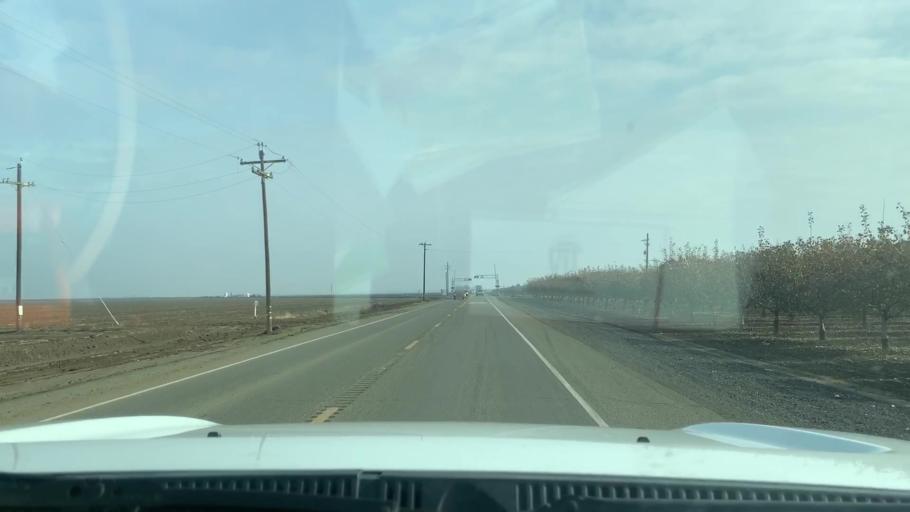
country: US
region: California
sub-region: Kings County
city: Lemoore Station
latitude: 36.2554
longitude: -119.9683
